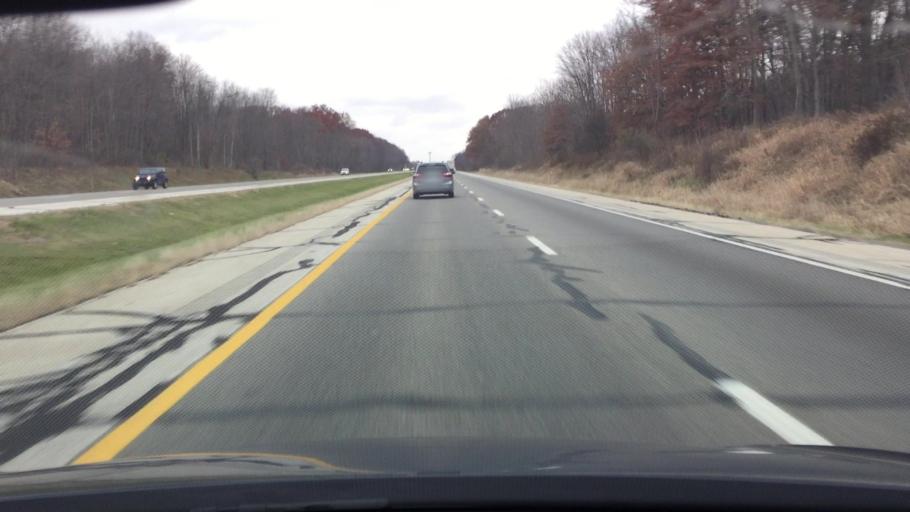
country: US
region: Ohio
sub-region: Mahoning County
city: Canfield
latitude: 41.0338
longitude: -80.7418
